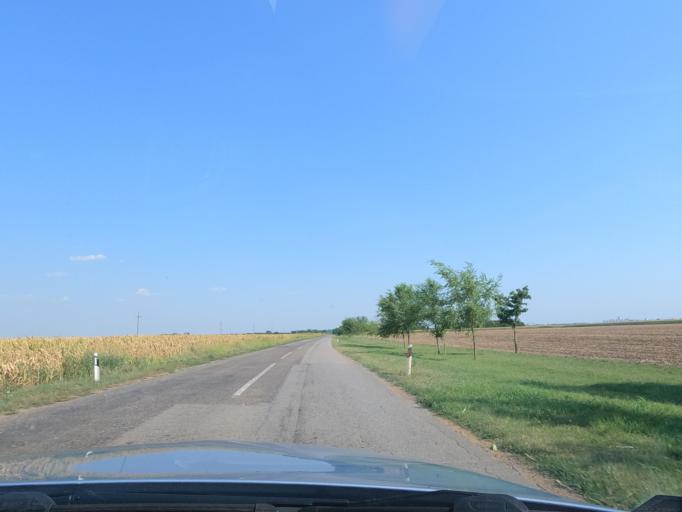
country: RS
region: Autonomna Pokrajina Vojvodina
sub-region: Juznobacki Okrug
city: Becej
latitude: 45.6410
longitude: 19.9959
